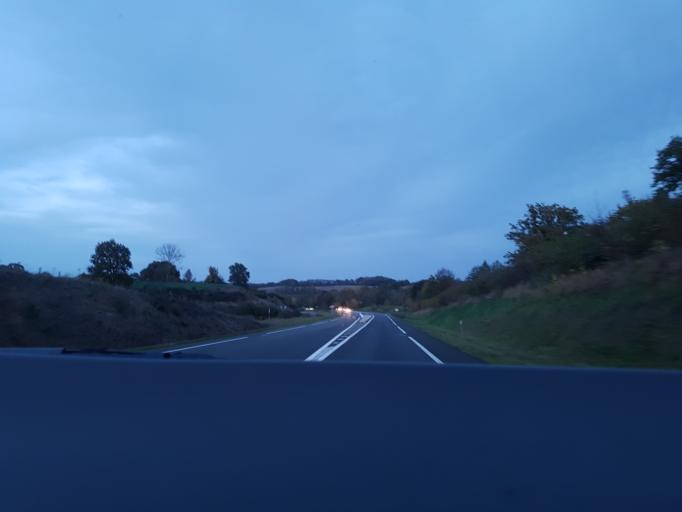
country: FR
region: Pays de la Loire
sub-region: Departement de la Mayenne
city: Montigne-le-Brillant
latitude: 48.0229
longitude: -0.8178
